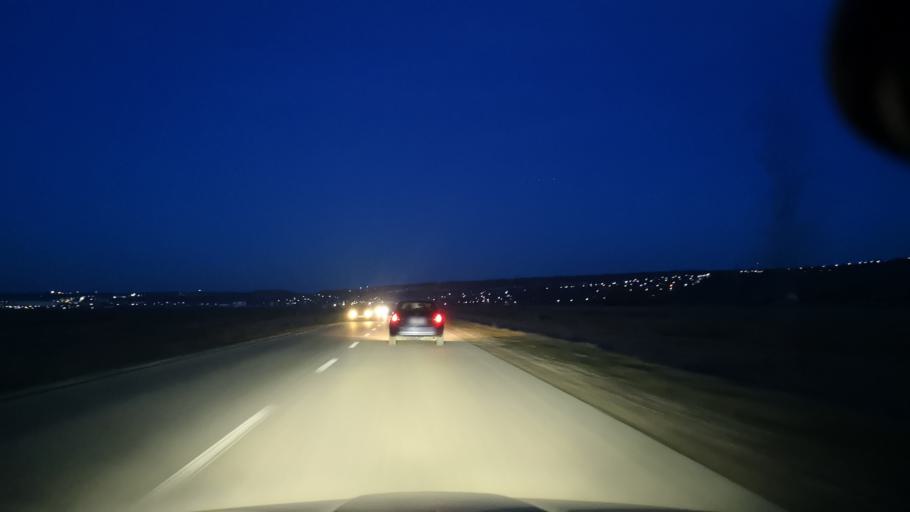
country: MD
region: Orhei
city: Orhei
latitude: 47.3450
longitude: 28.7842
